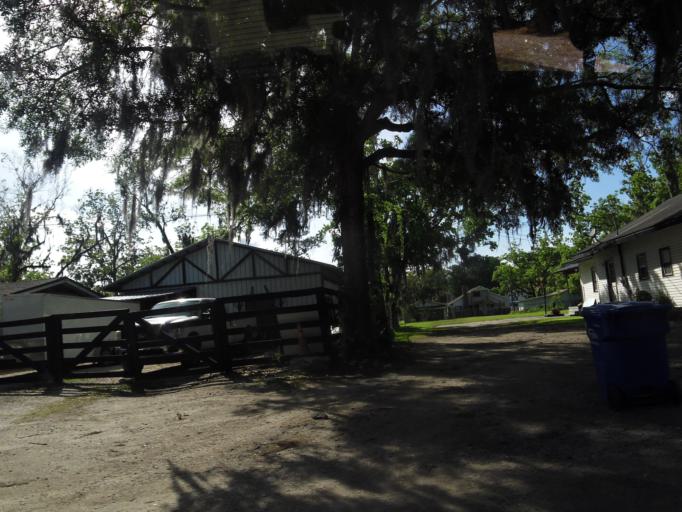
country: US
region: Florida
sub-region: Nassau County
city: Callahan
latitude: 30.5634
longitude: -81.8319
